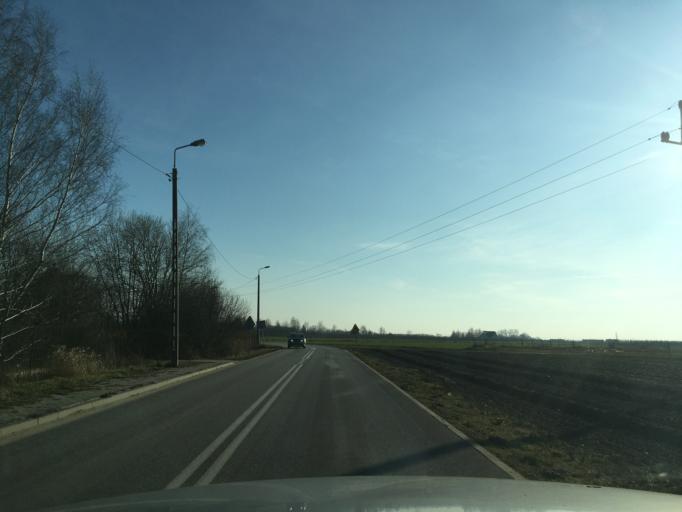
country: PL
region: Masovian Voivodeship
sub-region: Powiat pruszkowski
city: Nadarzyn
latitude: 52.0434
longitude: 20.8267
